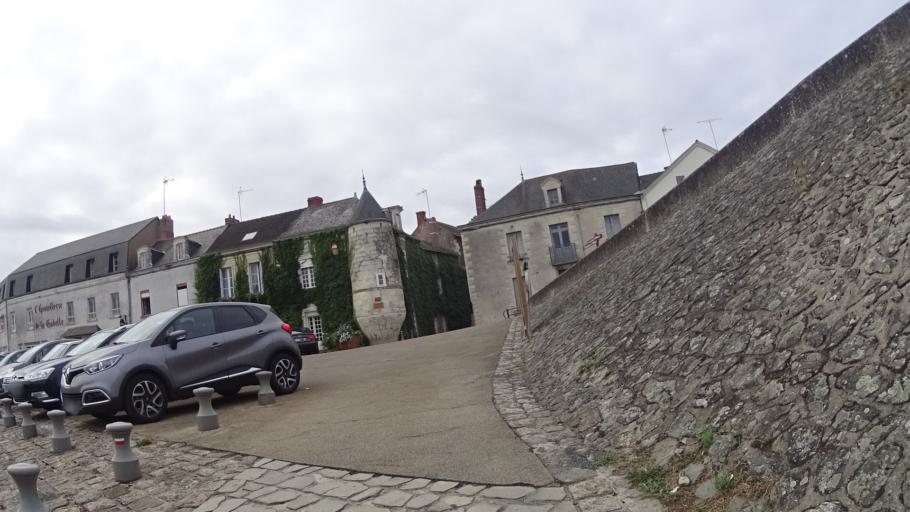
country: FR
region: Pays de la Loire
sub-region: Departement de Maine-et-Loire
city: Saint-Florent-le-Vieil
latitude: 47.3641
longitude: -1.0142
